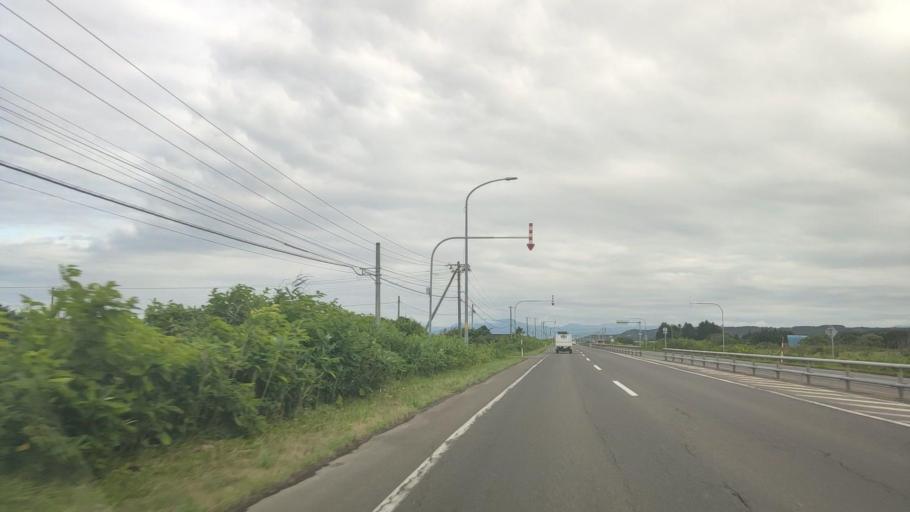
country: JP
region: Hokkaido
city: Niseko Town
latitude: 42.4086
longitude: 140.3062
